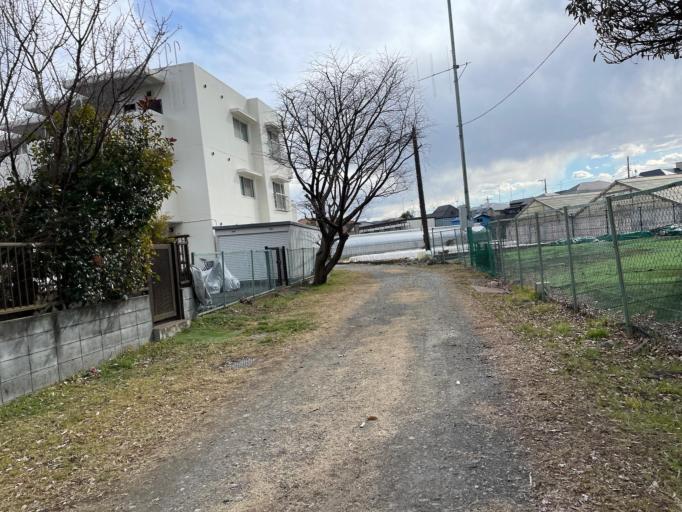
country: JP
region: Tokyo
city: Chofugaoka
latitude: 35.6578
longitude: 139.5197
